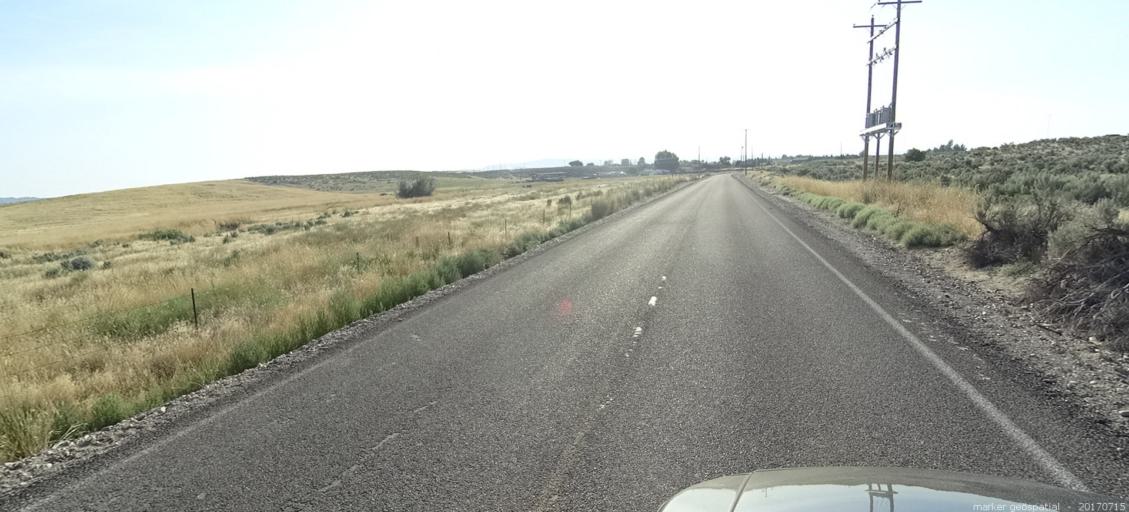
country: US
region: Idaho
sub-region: Ada County
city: Boise
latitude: 43.3894
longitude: -115.9792
